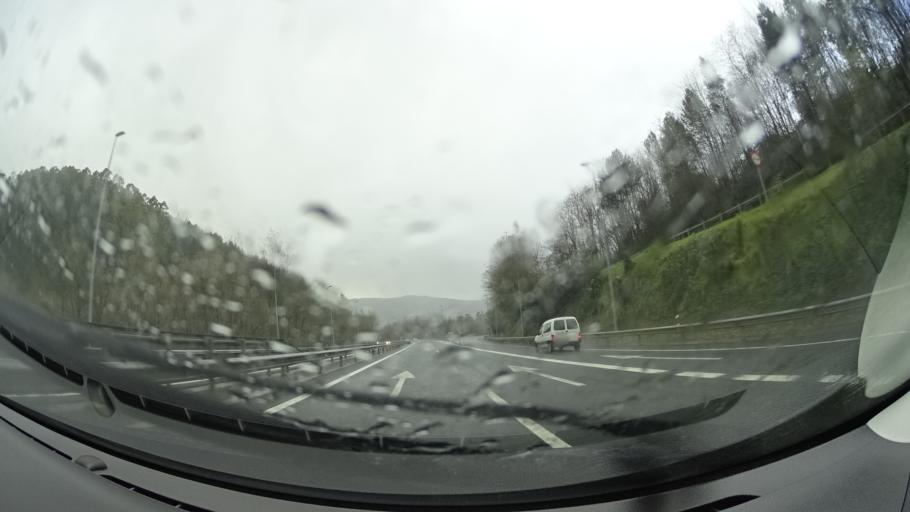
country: ES
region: Basque Country
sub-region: Bizkaia
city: Derio
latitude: 43.3113
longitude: -2.8795
